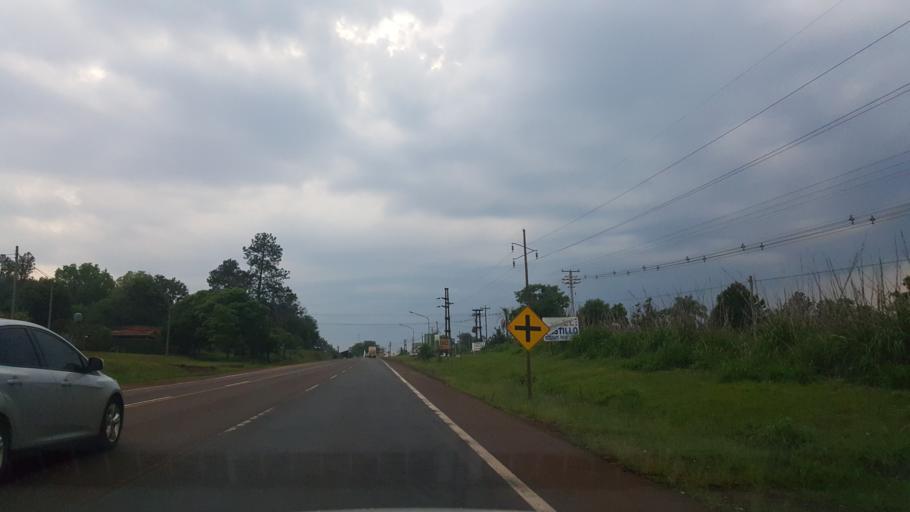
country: AR
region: Misiones
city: Capiovi
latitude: -26.9359
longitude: -55.0663
